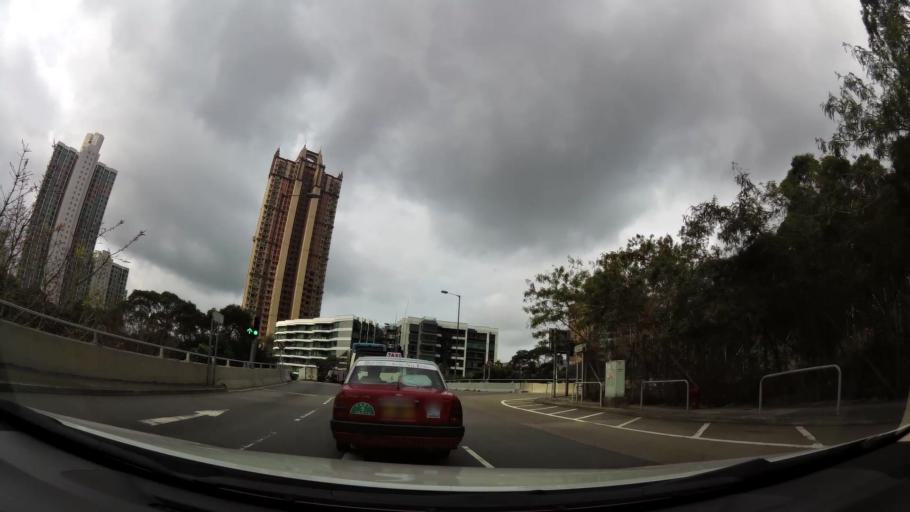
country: HK
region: Wong Tai Sin
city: Wong Tai Sin
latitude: 22.3436
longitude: 114.1850
